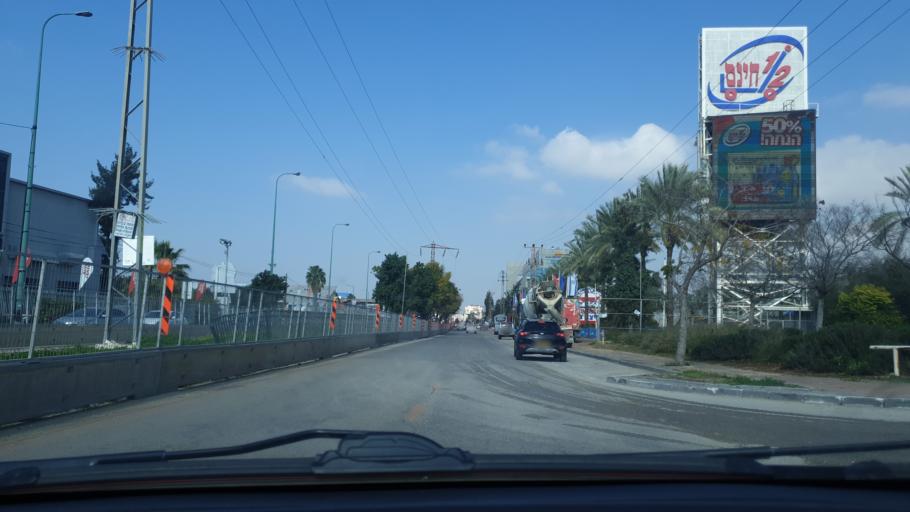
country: IL
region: Tel Aviv
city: Azor
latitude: 32.0084
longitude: 34.8079
